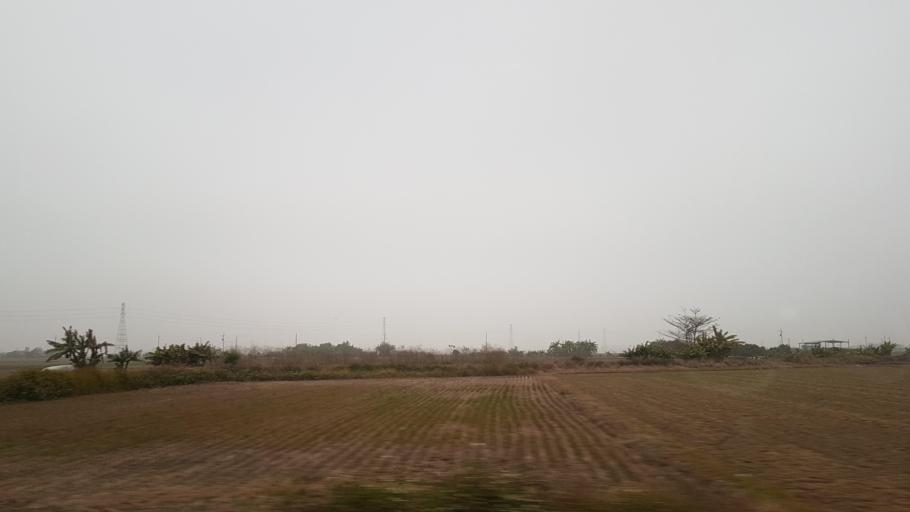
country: TW
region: Taiwan
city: Xinying
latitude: 23.3424
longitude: 120.3414
